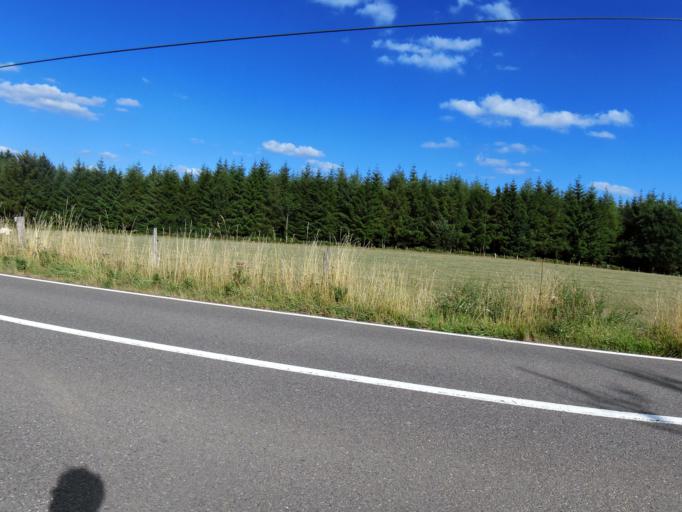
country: BE
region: Wallonia
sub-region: Province de Namur
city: Bievre
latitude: 49.9229
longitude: 5.0402
